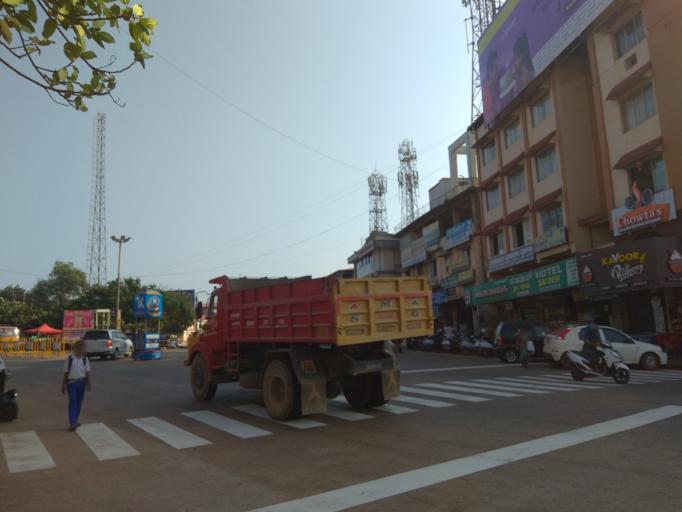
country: IN
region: Karnataka
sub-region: Dakshina Kannada
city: Mangalore
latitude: 12.9261
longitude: 74.8583
